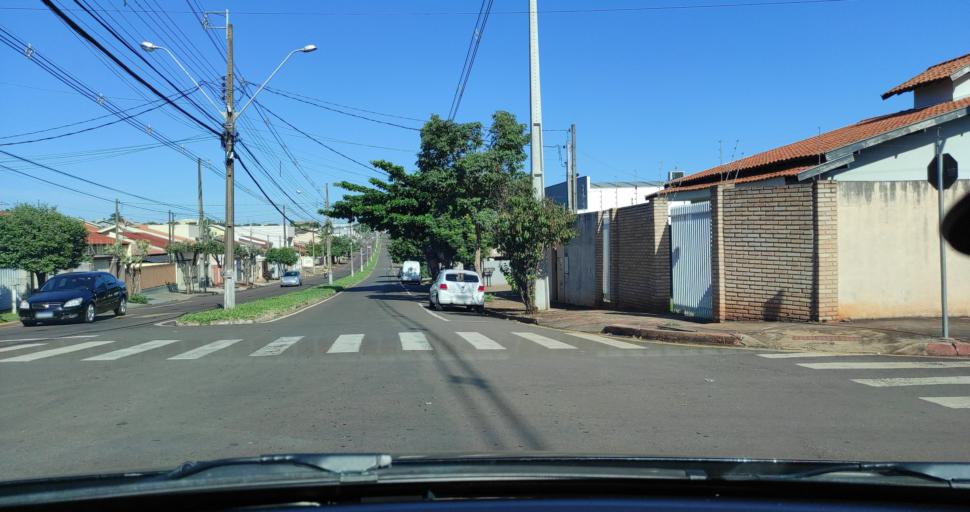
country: BR
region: Parana
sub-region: Ibipora
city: Ibipora
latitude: -23.2732
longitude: -51.0645
